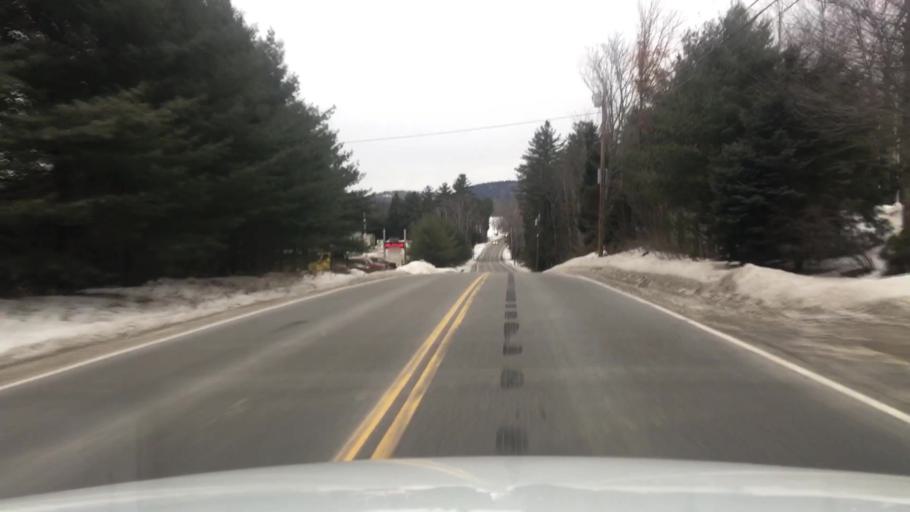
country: US
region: Maine
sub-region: York County
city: Limerick
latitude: 43.7104
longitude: -70.8117
